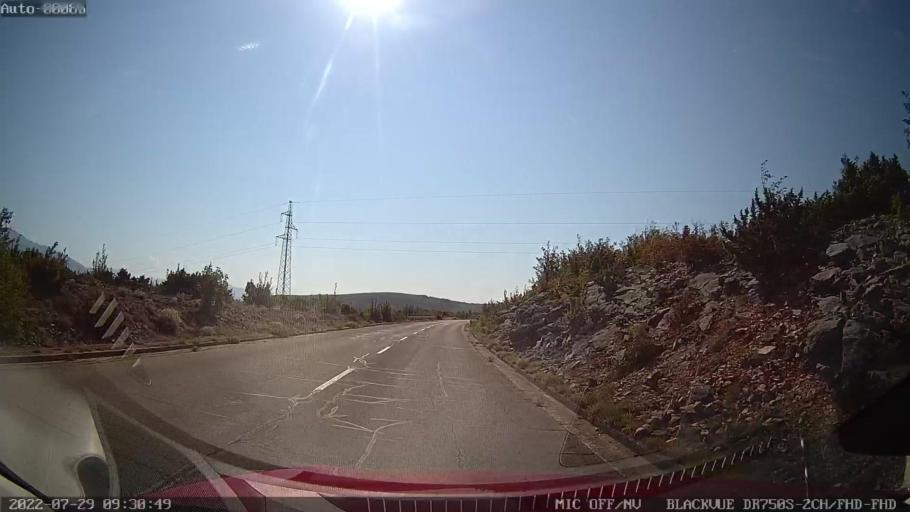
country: HR
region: Zadarska
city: Obrovac
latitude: 44.1926
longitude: 15.6909
